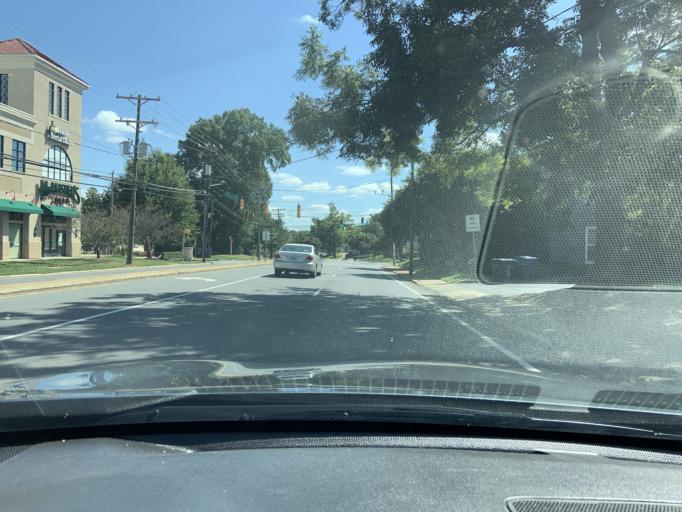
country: US
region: North Carolina
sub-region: Mecklenburg County
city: Charlotte
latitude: 35.1657
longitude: -80.8505
